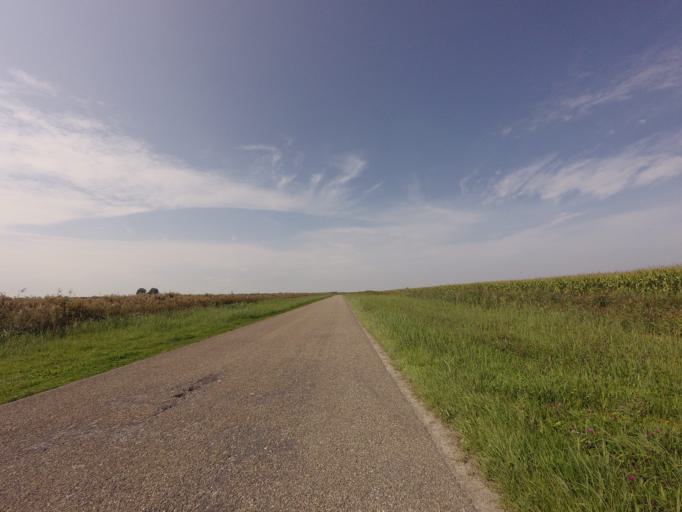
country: NL
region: Groningen
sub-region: Gemeente De Marne
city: Ulrum
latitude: 53.3424
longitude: 6.2859
